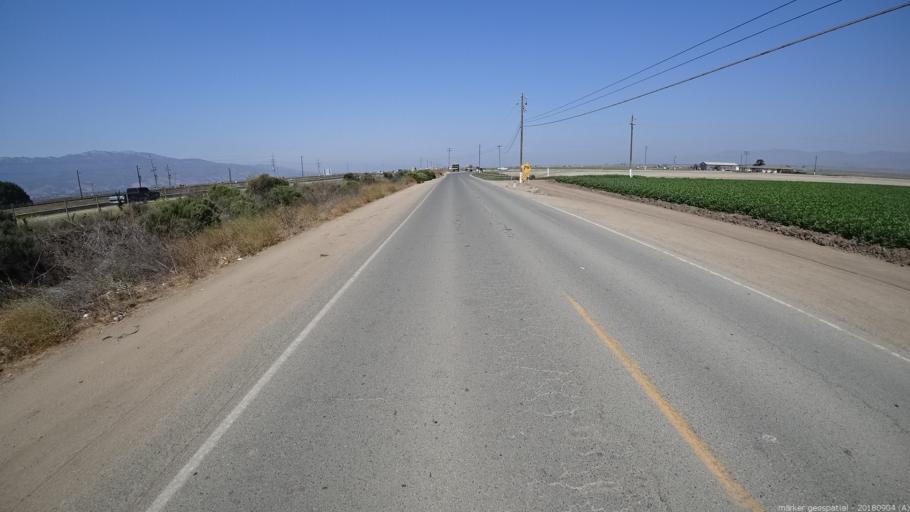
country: US
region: California
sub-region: Monterey County
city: Gonzales
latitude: 36.5292
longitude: -121.4718
